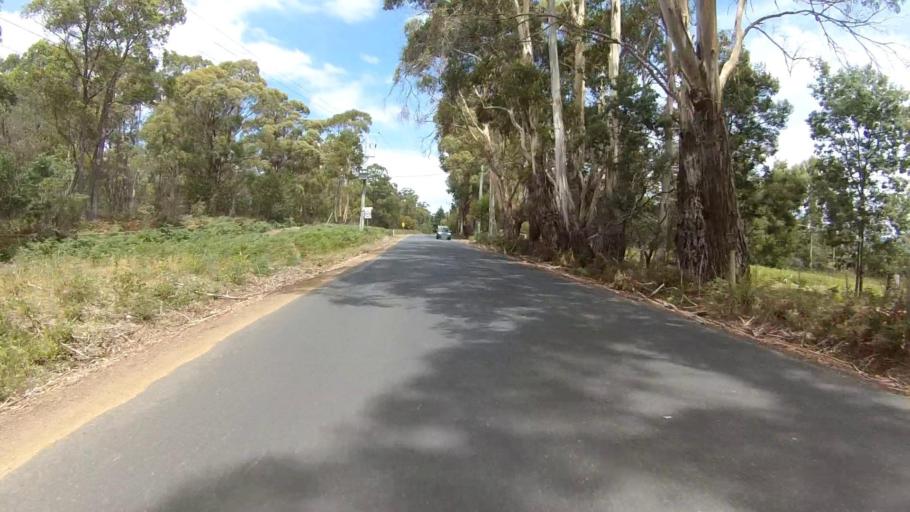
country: AU
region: Tasmania
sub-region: Kingborough
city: Blackmans Bay
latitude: -43.0102
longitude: 147.2880
